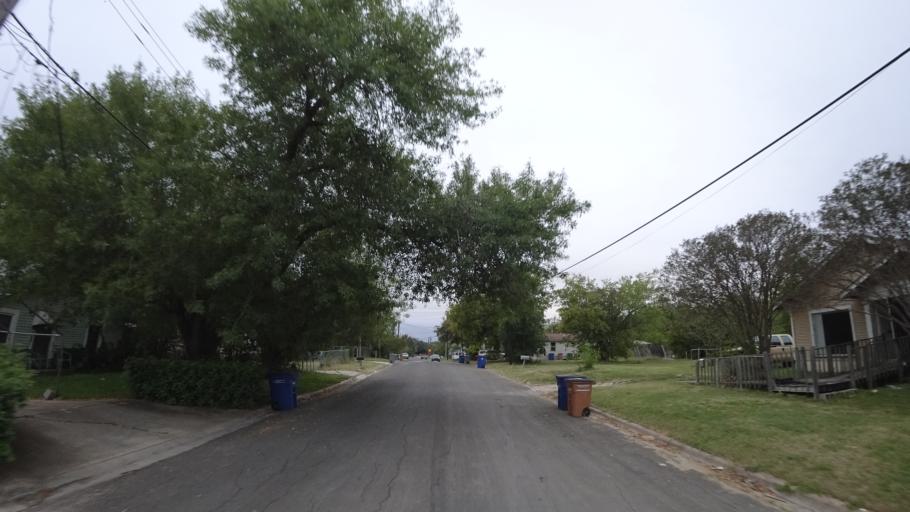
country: US
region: Texas
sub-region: Travis County
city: Austin
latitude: 30.2756
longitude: -97.6959
